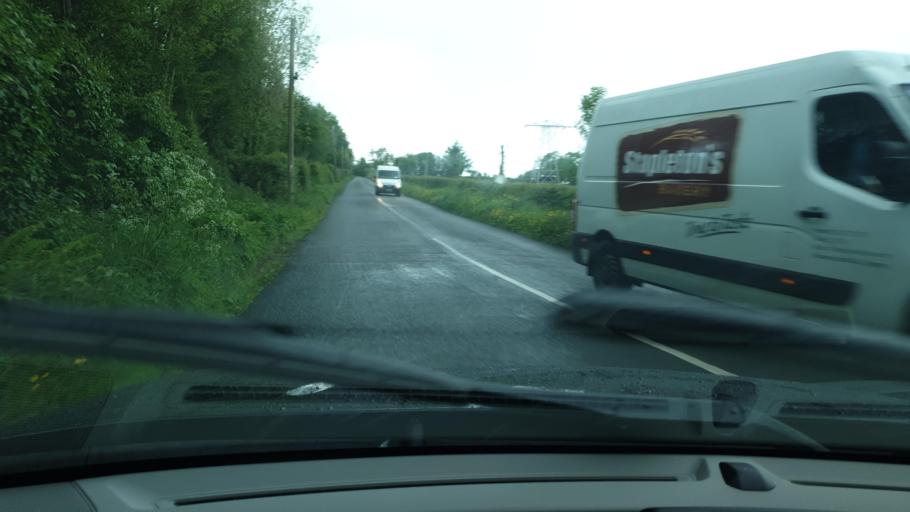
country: IE
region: Leinster
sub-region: Laois
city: Mountrath
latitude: 53.0660
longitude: -7.4070
